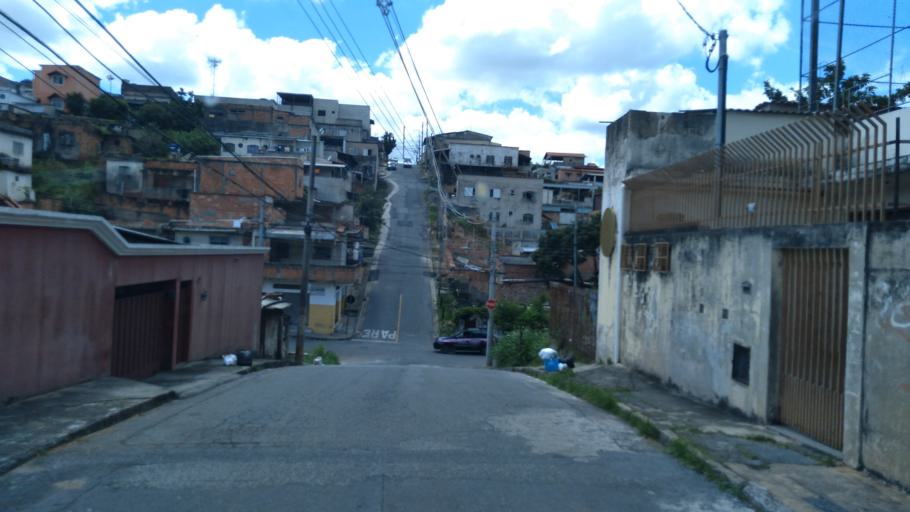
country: BR
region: Minas Gerais
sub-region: Belo Horizonte
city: Belo Horizonte
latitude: -19.8707
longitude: -43.9098
